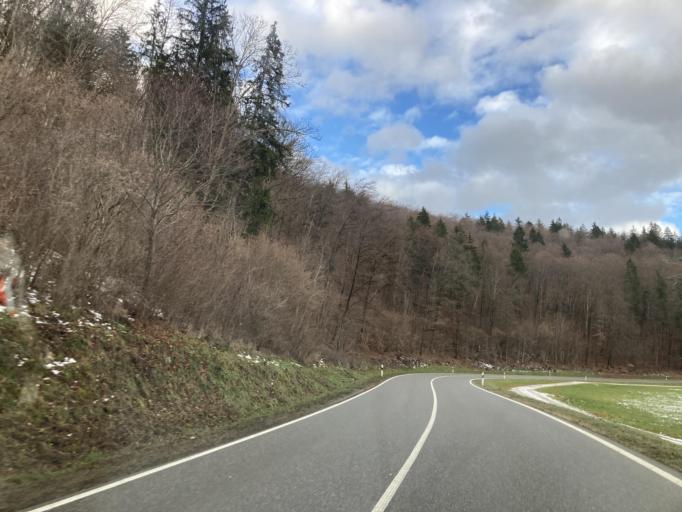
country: DE
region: Baden-Wuerttemberg
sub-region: Freiburg Region
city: Fridingen an der Donau
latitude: 48.0132
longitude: 8.9029
